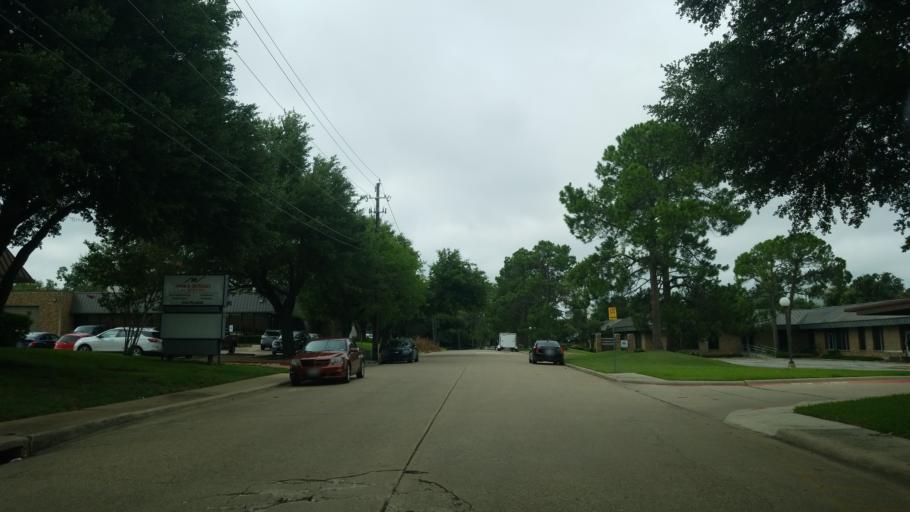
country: US
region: Texas
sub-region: Dallas County
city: University Park
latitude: 32.8350
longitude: -96.8715
